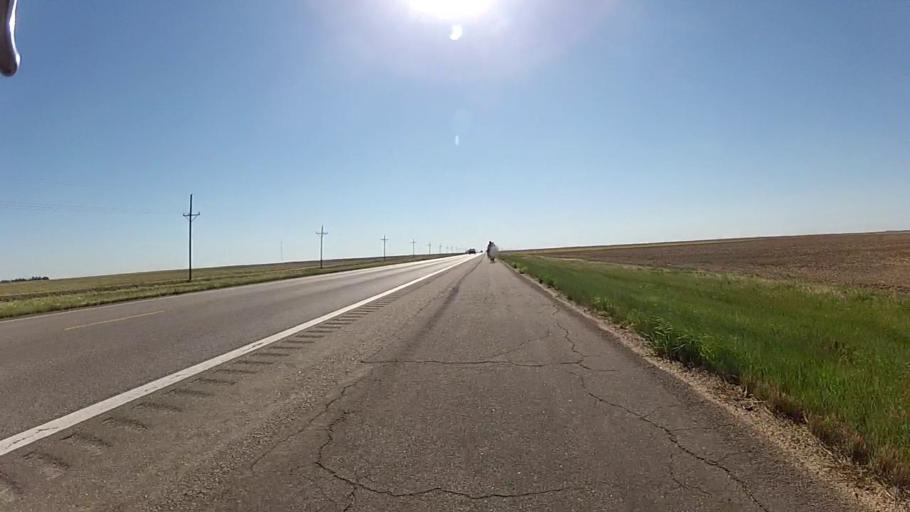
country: US
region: Kansas
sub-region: Kiowa County
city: Greensburg
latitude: 37.5862
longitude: -99.6305
